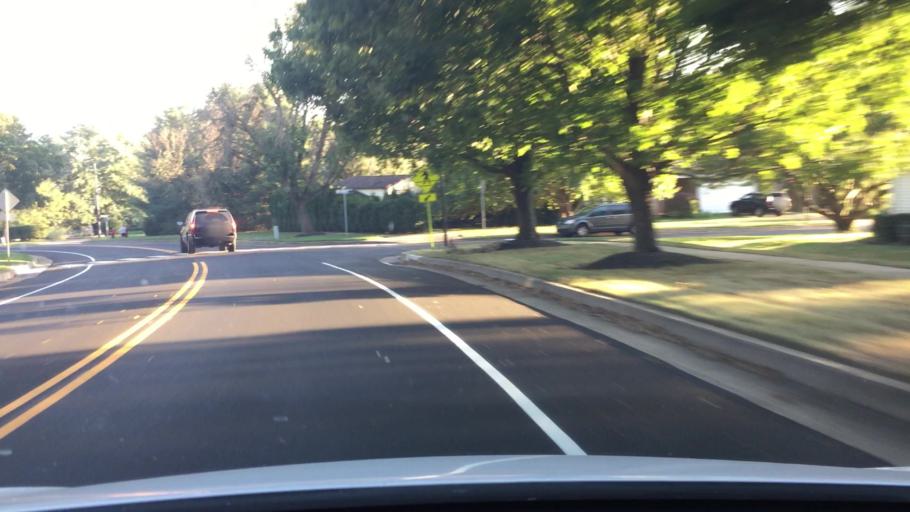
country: US
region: Pennsylvania
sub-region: Bucks County
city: Newtown
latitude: 40.2172
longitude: -74.9518
